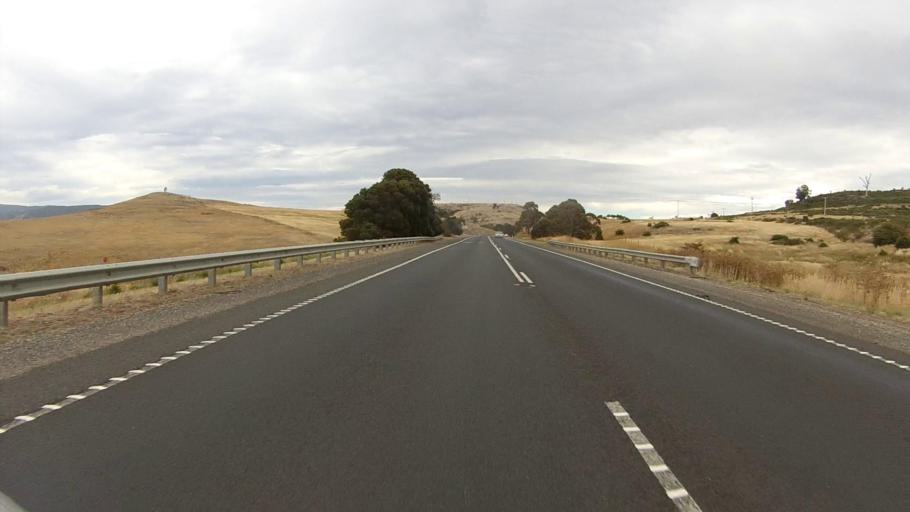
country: AU
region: Tasmania
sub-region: Brighton
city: Bridgewater
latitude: -42.3494
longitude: 147.3375
